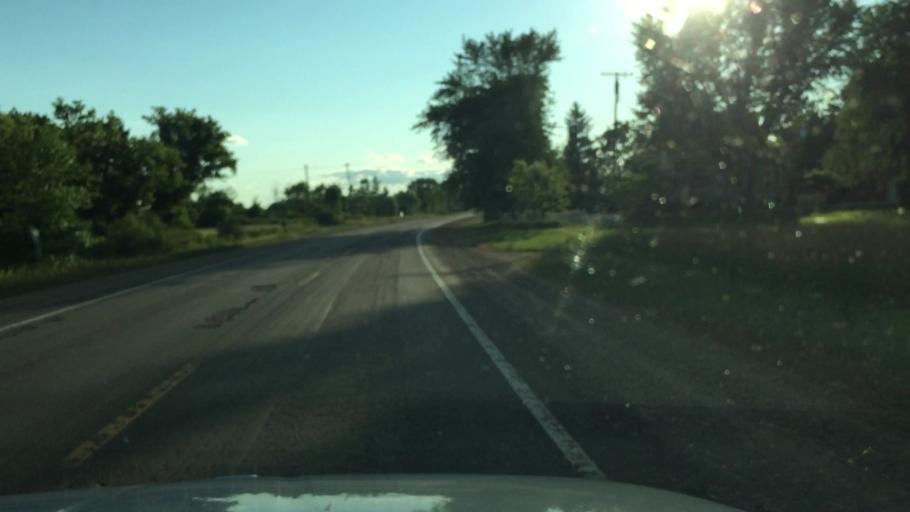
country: US
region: Michigan
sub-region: Lapeer County
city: Imlay City
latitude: 43.0250
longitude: -83.0060
